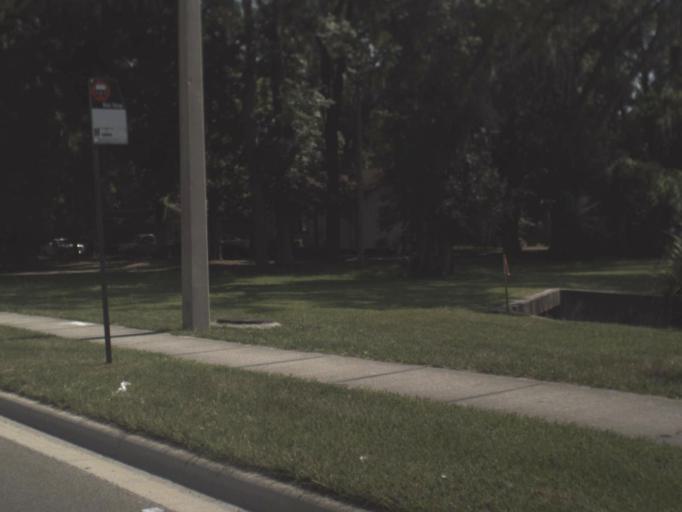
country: US
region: Florida
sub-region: Duval County
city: Jacksonville
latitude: 30.3183
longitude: -81.7519
